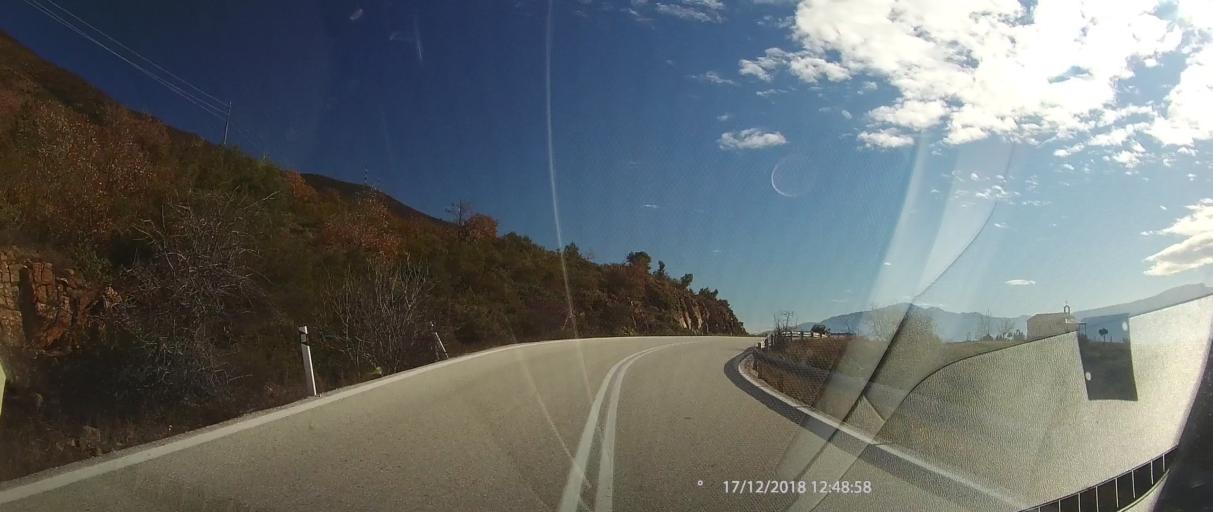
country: GR
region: Thessaly
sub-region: Trikala
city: Kastraki
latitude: 39.7814
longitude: 21.4405
